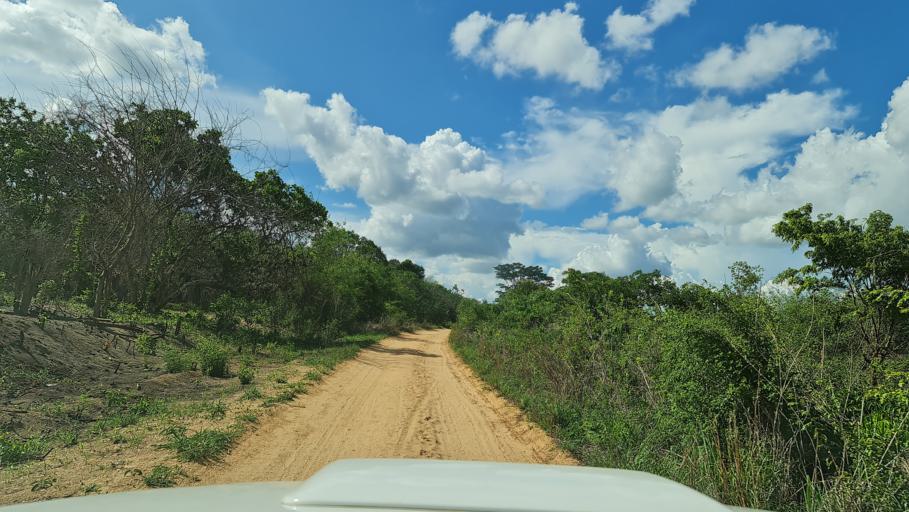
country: MZ
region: Nampula
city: Ilha de Mocambique
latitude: -15.4341
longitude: 40.2760
